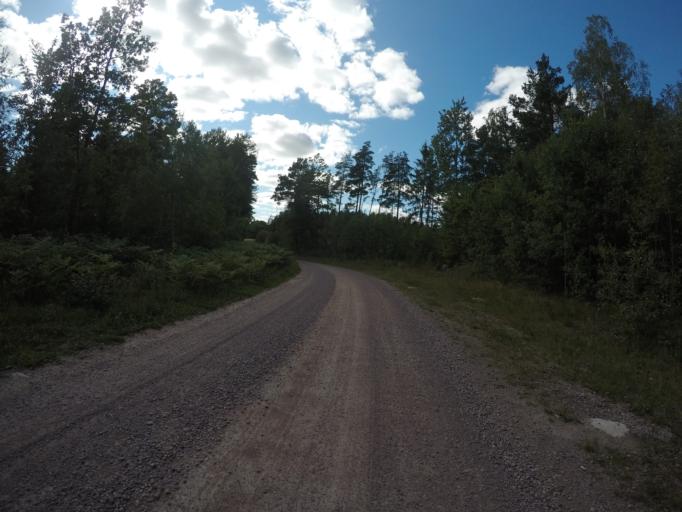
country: SE
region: Vaestmanland
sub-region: Hallstahammars Kommun
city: Kolback
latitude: 59.4936
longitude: 16.2043
